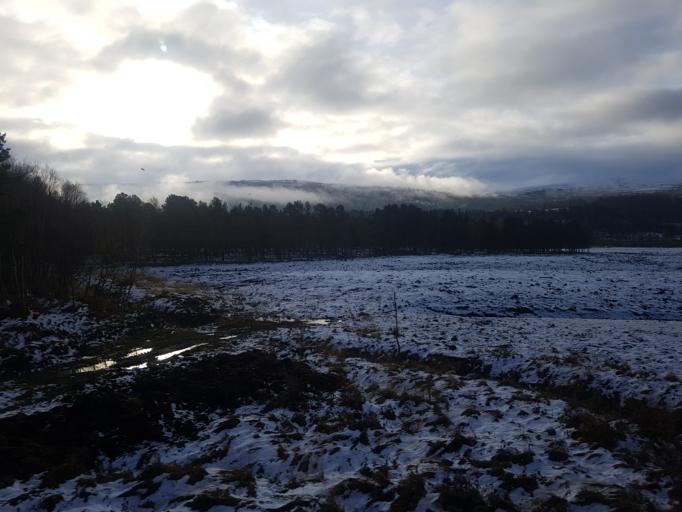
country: NO
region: Sor-Trondelag
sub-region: Oppdal
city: Oppdal
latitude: 62.6362
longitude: 9.8010
